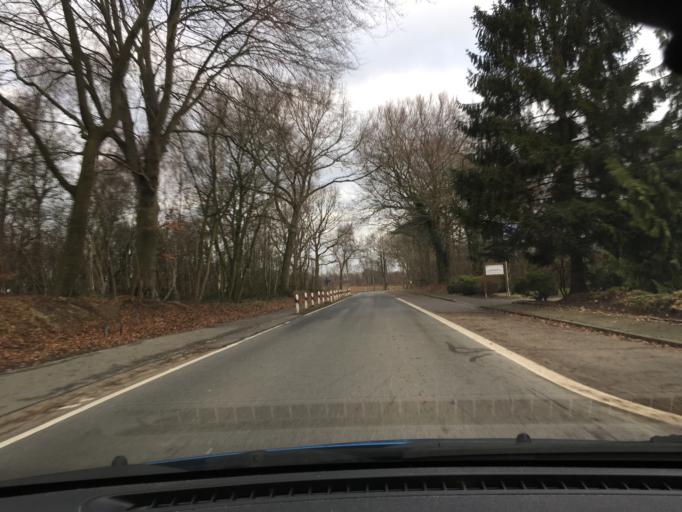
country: DE
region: Schleswig-Holstein
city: Schenefeld
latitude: 54.0472
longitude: 9.4668
